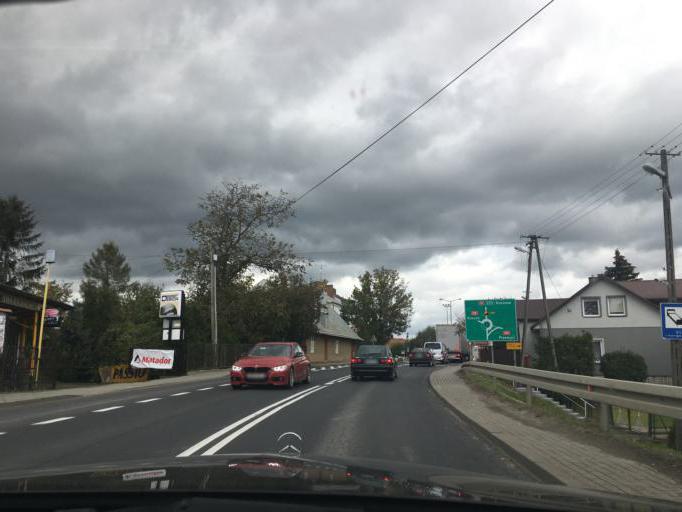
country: PL
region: Subcarpathian Voivodeship
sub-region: Powiat krosnienski
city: Miejsce Piastowe
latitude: 49.6339
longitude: 21.7856
